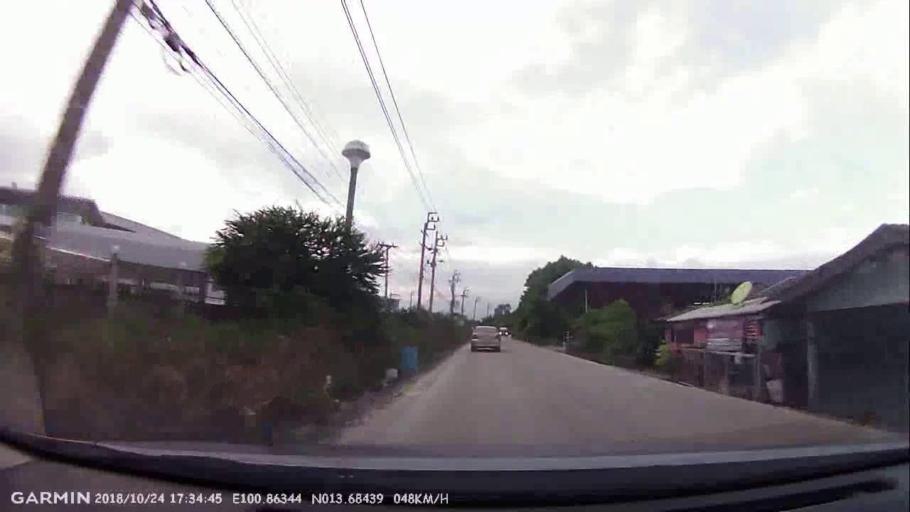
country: TH
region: Samut Prakan
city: Ban Khlong Bang Sao Thong
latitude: 13.6845
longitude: 100.8634
